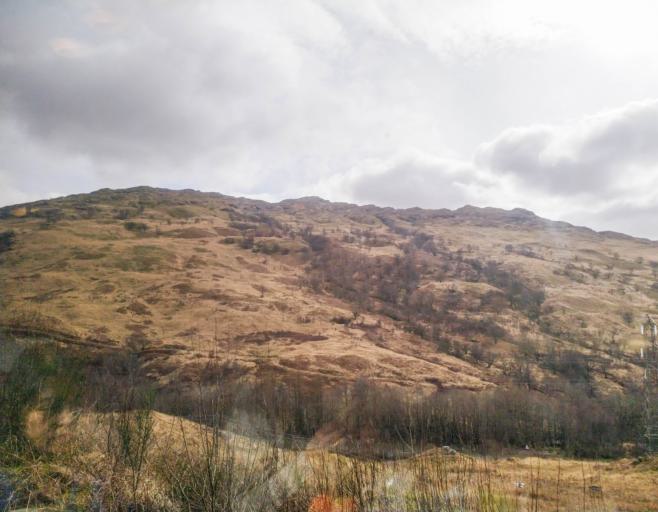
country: GB
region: Scotland
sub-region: Argyll and Bute
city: Garelochhead
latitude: 56.3514
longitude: -4.6973
